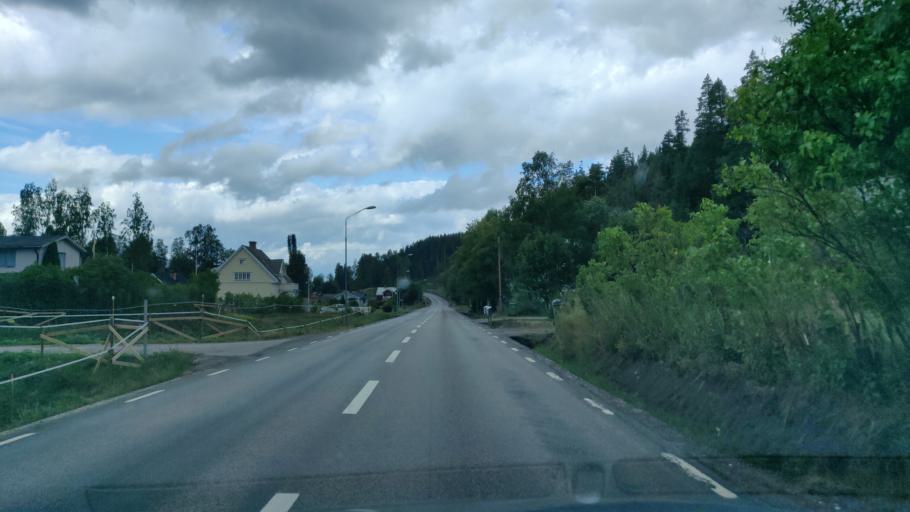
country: SE
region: Vaermland
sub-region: Torsby Kommun
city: Torsby
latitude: 60.6179
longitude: 13.0393
